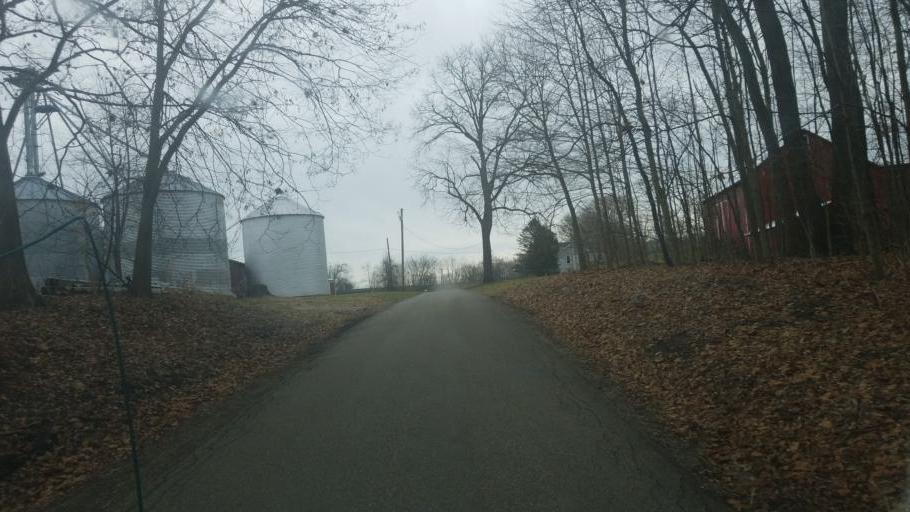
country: US
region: Ohio
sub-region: Richland County
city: Lincoln Heights
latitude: 40.7001
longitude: -82.3812
